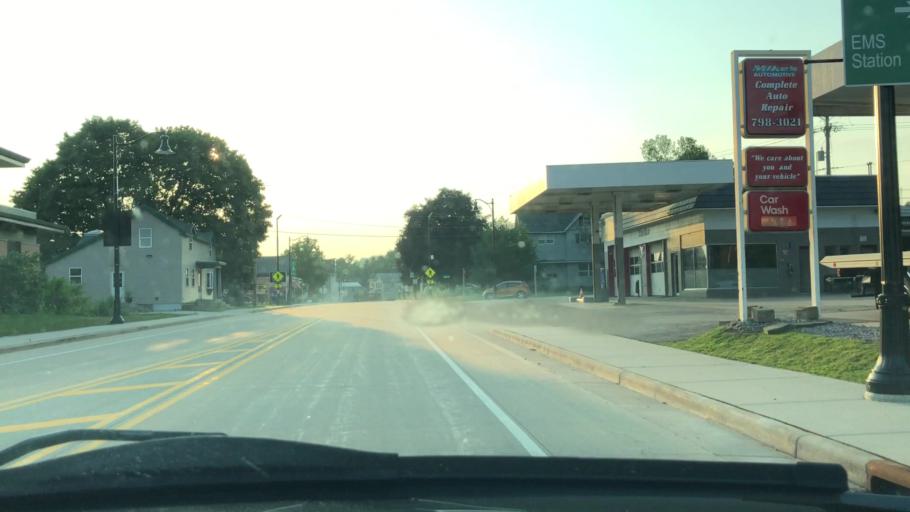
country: US
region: Wisconsin
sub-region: Dane County
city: Cross Plains
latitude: 43.1127
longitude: -89.6475
